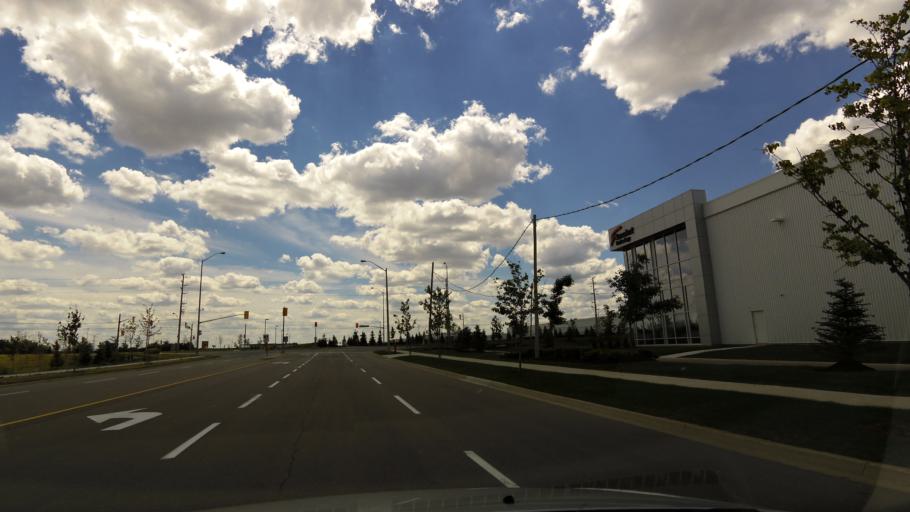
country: CA
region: Ontario
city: Brampton
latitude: 43.6161
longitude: -79.7831
